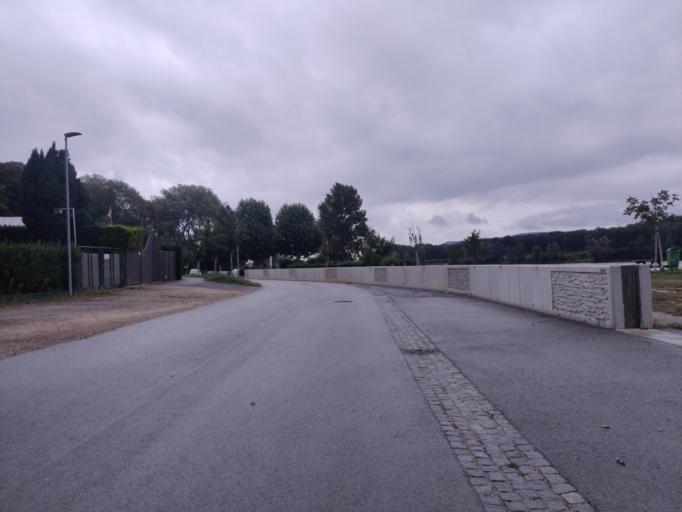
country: AT
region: Lower Austria
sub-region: Politischer Bezirk Korneuburg
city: Korneuburg
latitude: 48.3384
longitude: 16.3221
